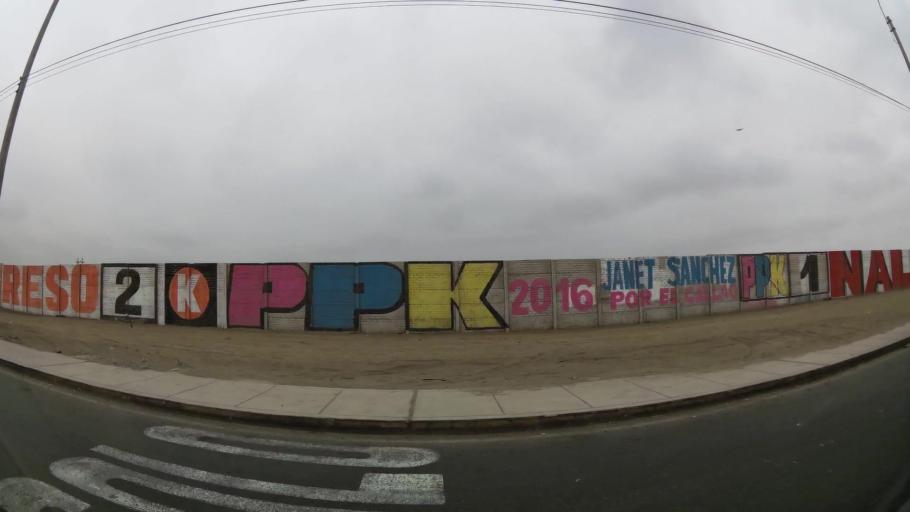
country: PE
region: Callao
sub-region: Callao
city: Callao
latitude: -12.0290
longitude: -77.1277
